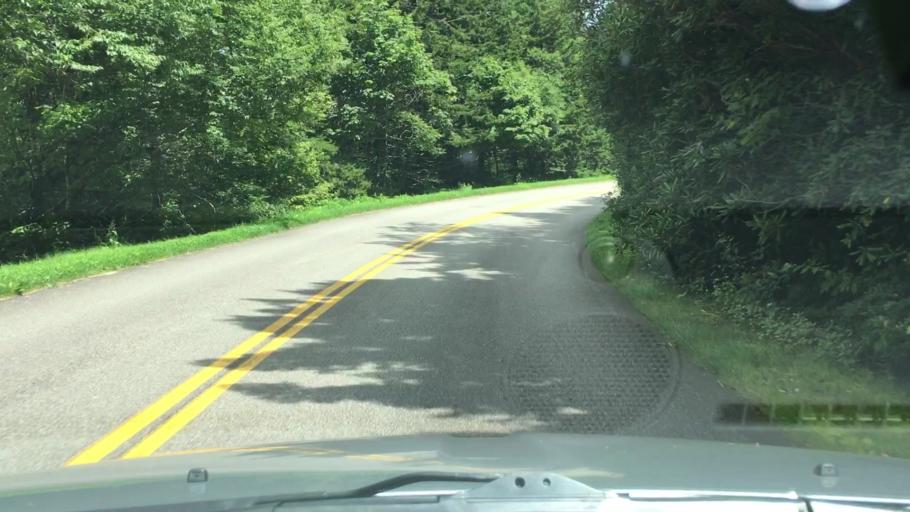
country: US
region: North Carolina
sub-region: Buncombe County
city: Black Mountain
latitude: 35.7084
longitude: -82.2643
